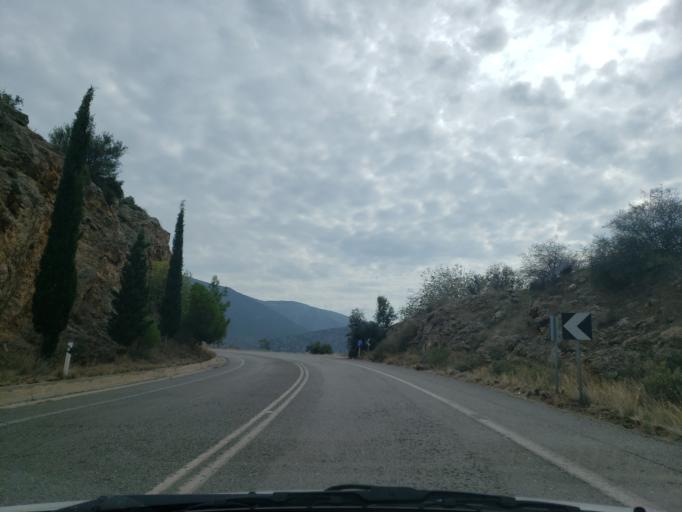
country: GR
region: Central Greece
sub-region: Nomos Fokidos
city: Delphi
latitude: 38.4734
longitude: 22.4562
